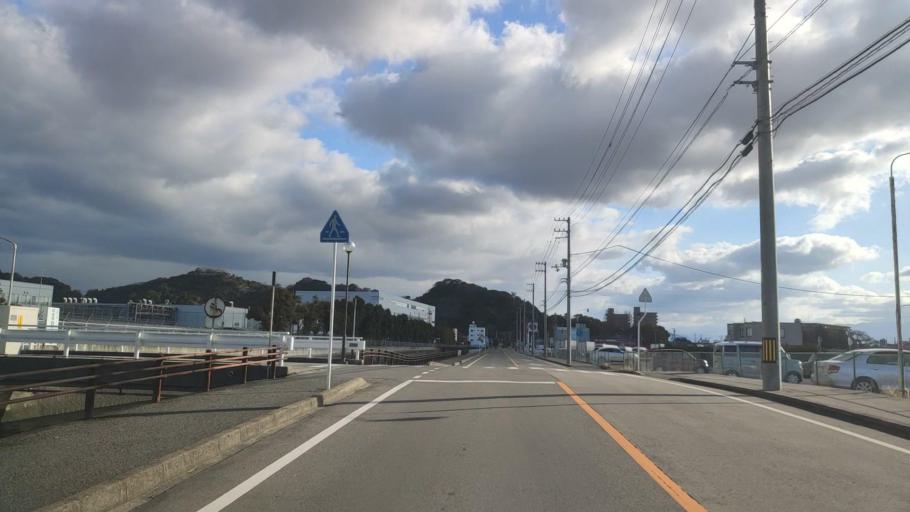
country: JP
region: Ehime
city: Masaki-cho
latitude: 33.8309
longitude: 132.7026
